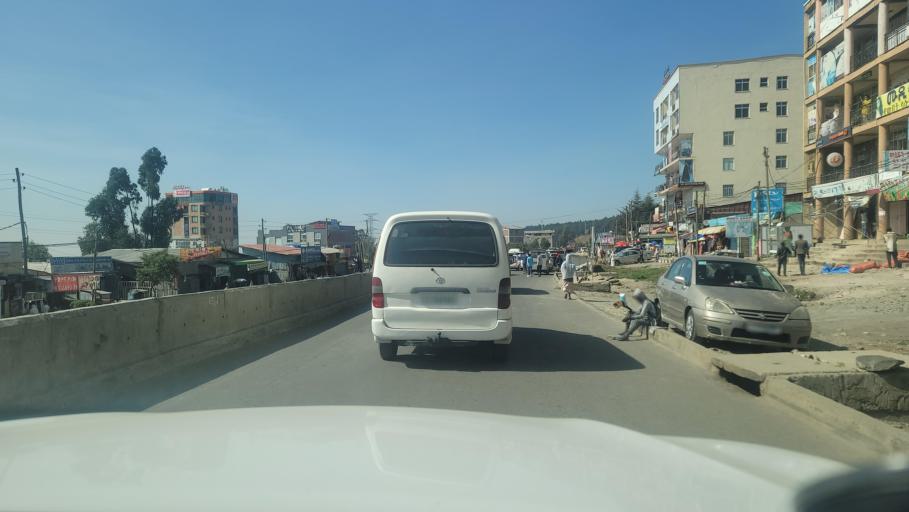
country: ET
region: Adis Abeba
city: Addis Ababa
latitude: 9.0361
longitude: 38.8290
